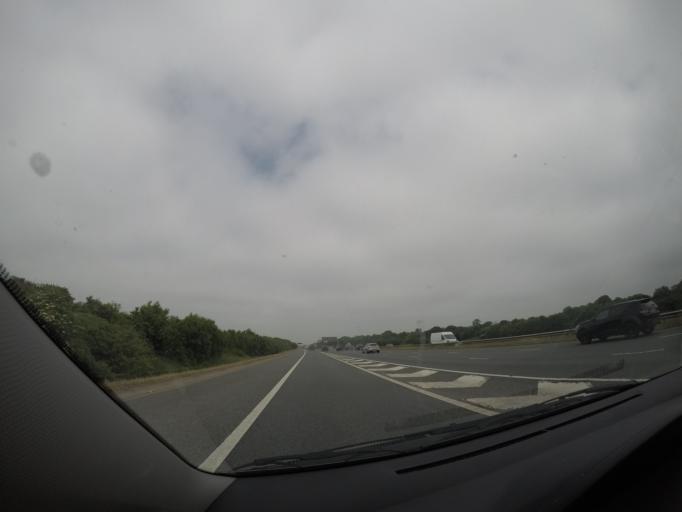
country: GB
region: England
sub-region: North Yorkshire
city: Boroughbridge
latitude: 54.0116
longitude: -1.3797
